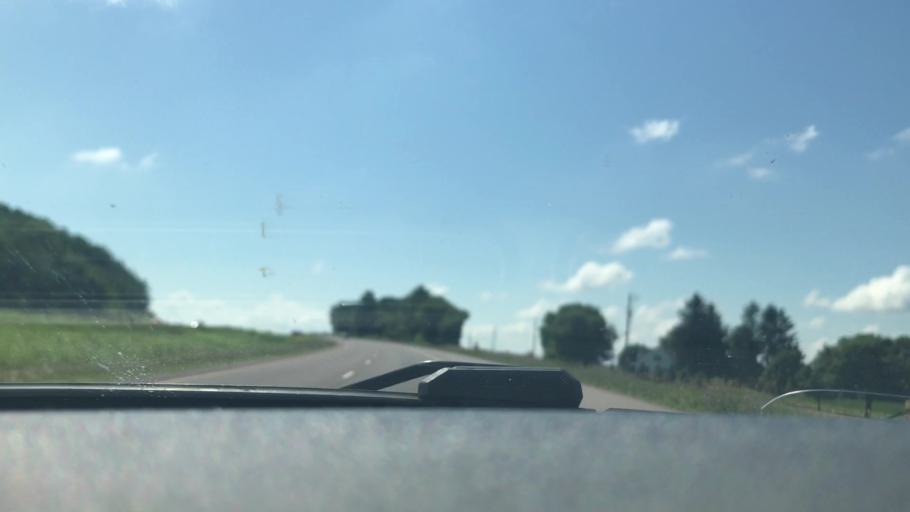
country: US
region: Wisconsin
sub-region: Chippewa County
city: Bloomer
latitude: 45.0467
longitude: -91.4647
